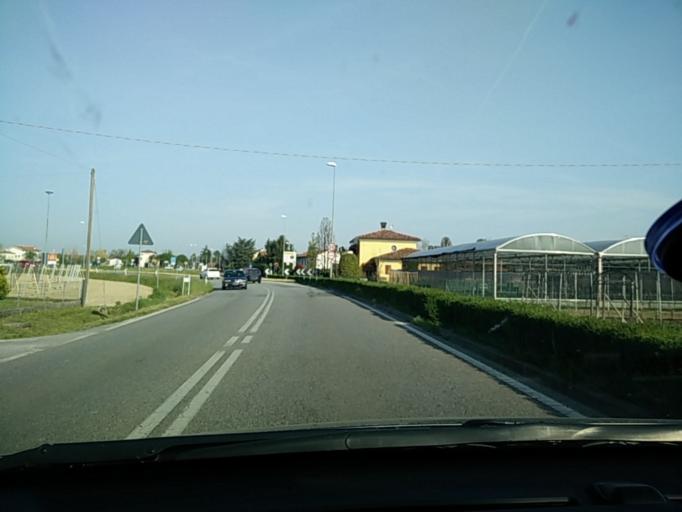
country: IT
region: Veneto
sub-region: Provincia di Treviso
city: Piavon
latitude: 45.7700
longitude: 12.5175
